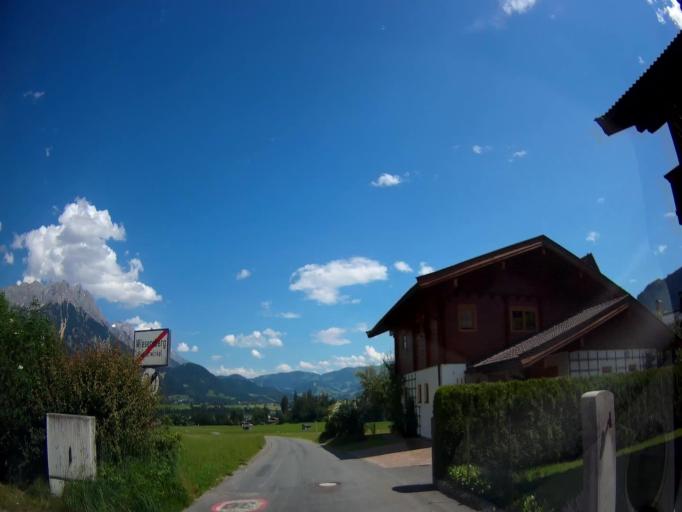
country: AT
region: Salzburg
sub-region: Politischer Bezirk Zell am See
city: Leogang
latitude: 47.4505
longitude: 12.7964
